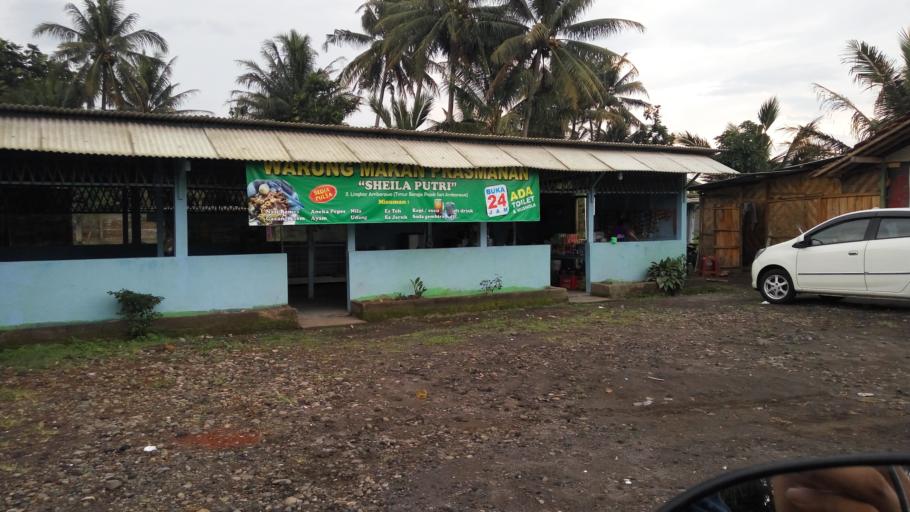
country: ID
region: Central Java
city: Ambarawa
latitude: -7.2730
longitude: 110.4050
